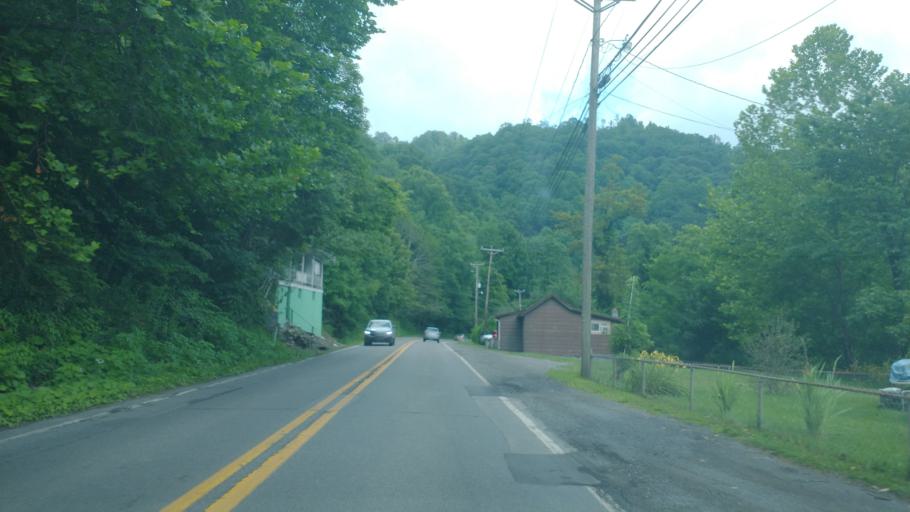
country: US
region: West Virginia
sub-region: McDowell County
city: Welch
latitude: 37.4056
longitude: -81.4236
